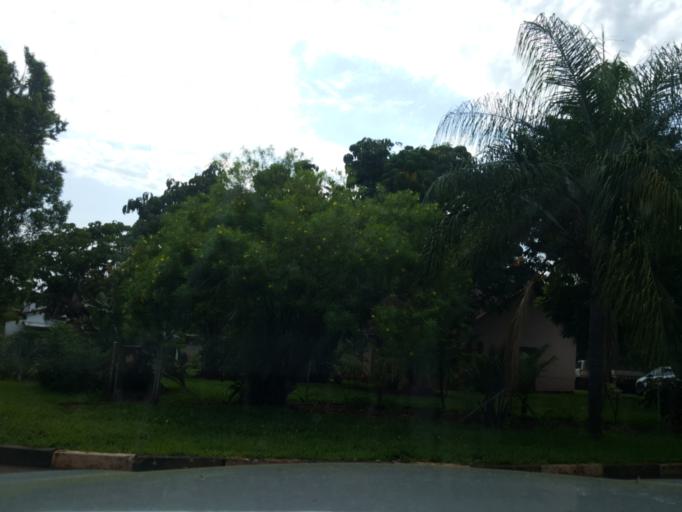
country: SZ
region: Hhohho
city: Ntfonjeni
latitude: -25.4936
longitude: 31.5110
